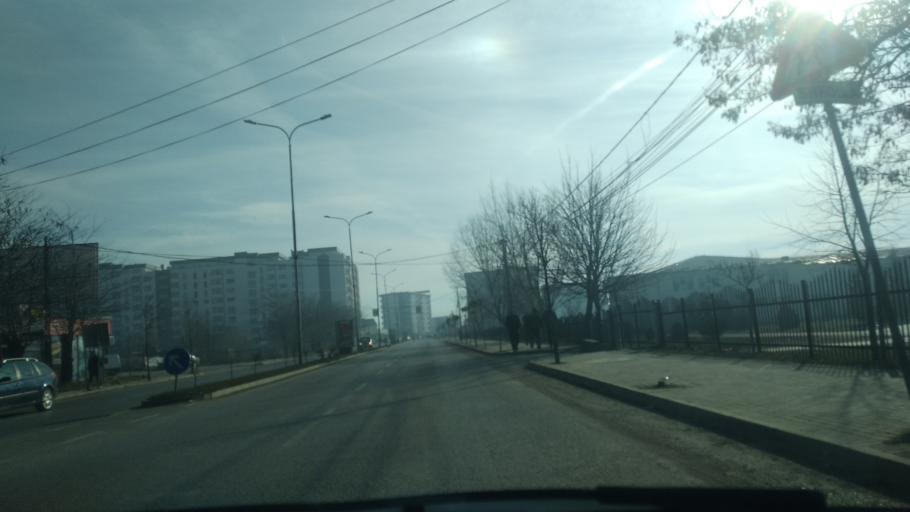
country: XK
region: Mitrovica
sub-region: Vushtrri
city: Vushtrri
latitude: 42.8197
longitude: 20.9772
